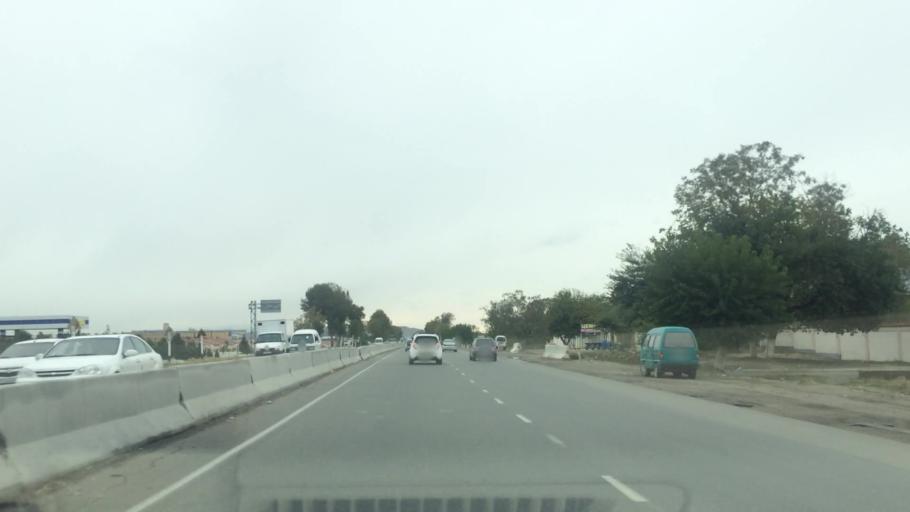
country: UZ
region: Samarqand
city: Jomboy
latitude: 39.7141
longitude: 67.1009
